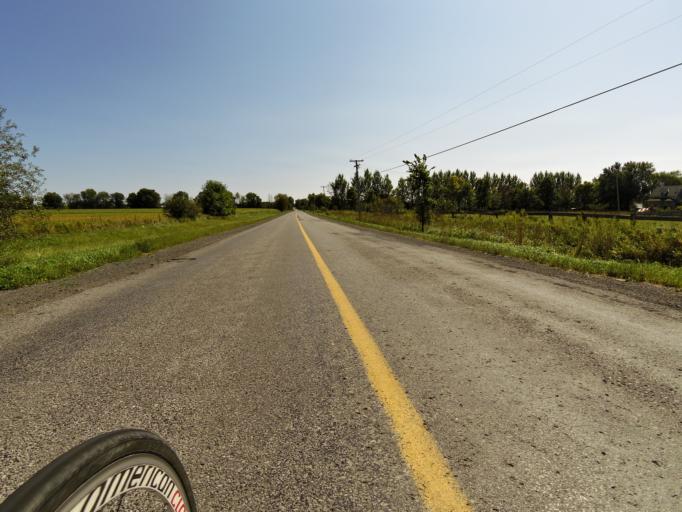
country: CA
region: Ontario
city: Bells Corners
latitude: 45.4278
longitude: -76.0535
